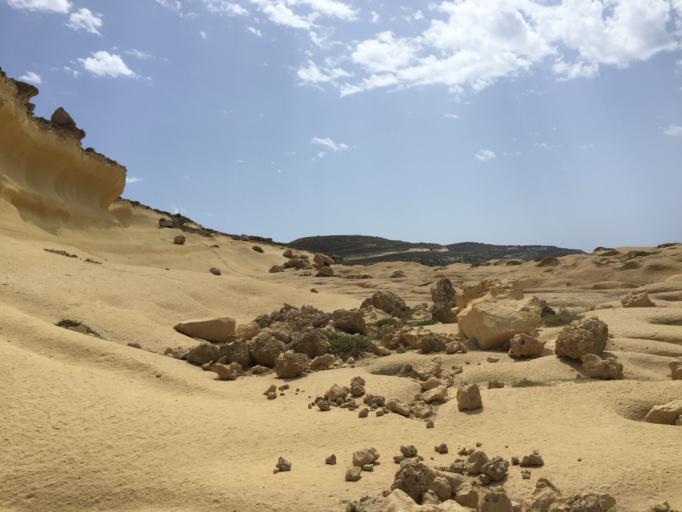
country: MT
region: L-Gharb
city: Gharb
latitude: 36.0764
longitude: 14.2023
